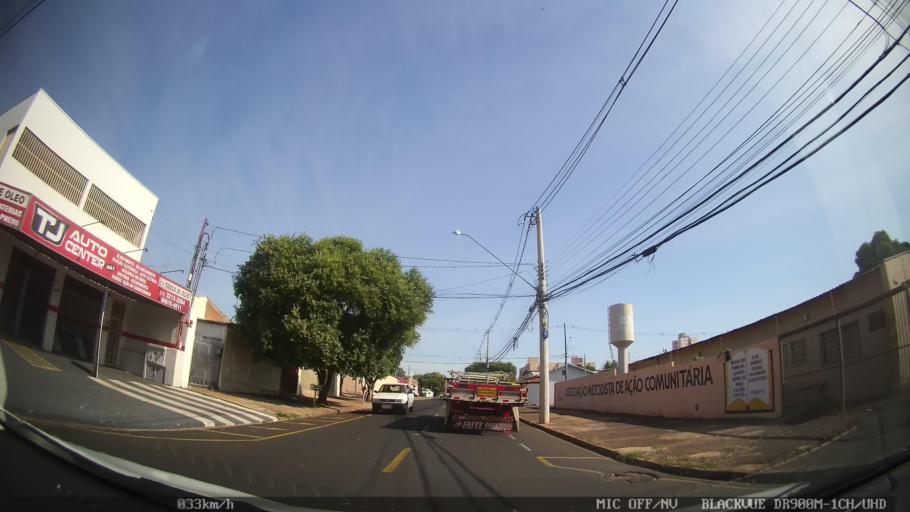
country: BR
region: Sao Paulo
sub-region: Sao Jose Do Rio Preto
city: Sao Jose do Rio Preto
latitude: -20.7955
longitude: -49.4090
